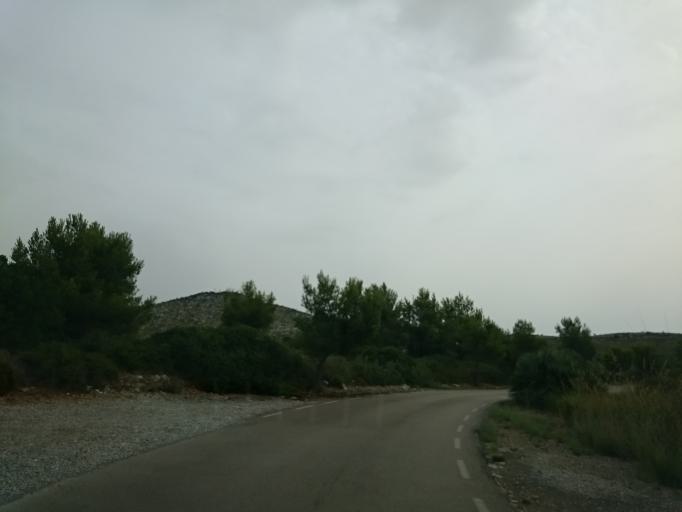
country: ES
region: Catalonia
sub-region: Provincia de Barcelona
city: Begues
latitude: 41.2823
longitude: 1.9062
